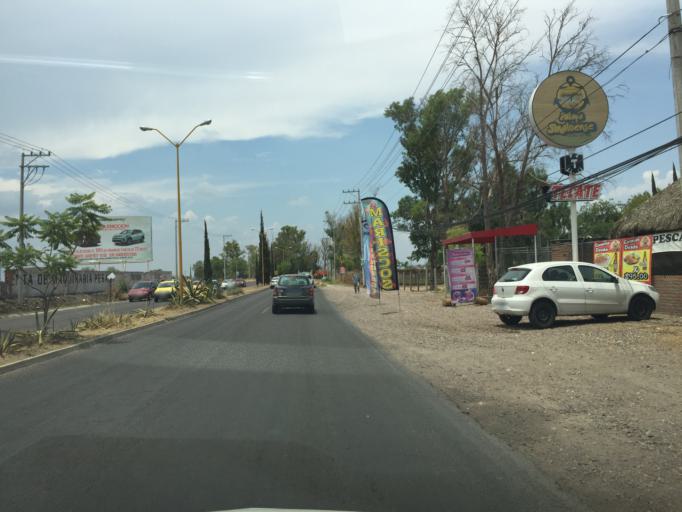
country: MX
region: Aguascalientes
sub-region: Aguascalientes
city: La Loma de los Negritos
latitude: 21.8611
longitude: -102.3388
